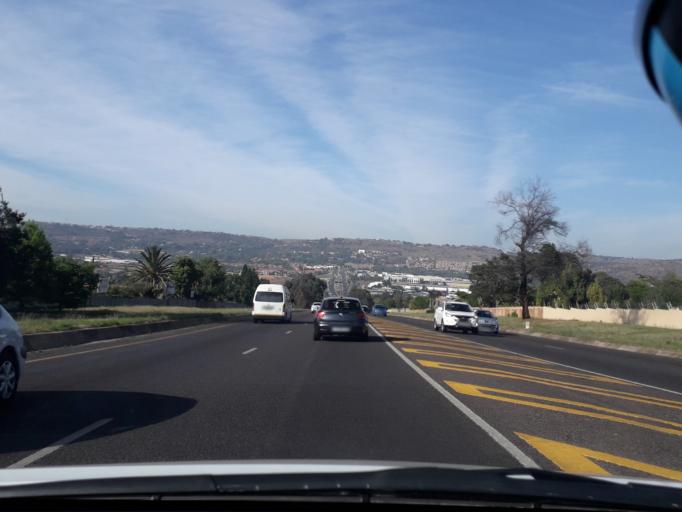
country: ZA
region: Gauteng
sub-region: City of Johannesburg Metropolitan Municipality
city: Roodepoort
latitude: -26.1139
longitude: 27.9180
